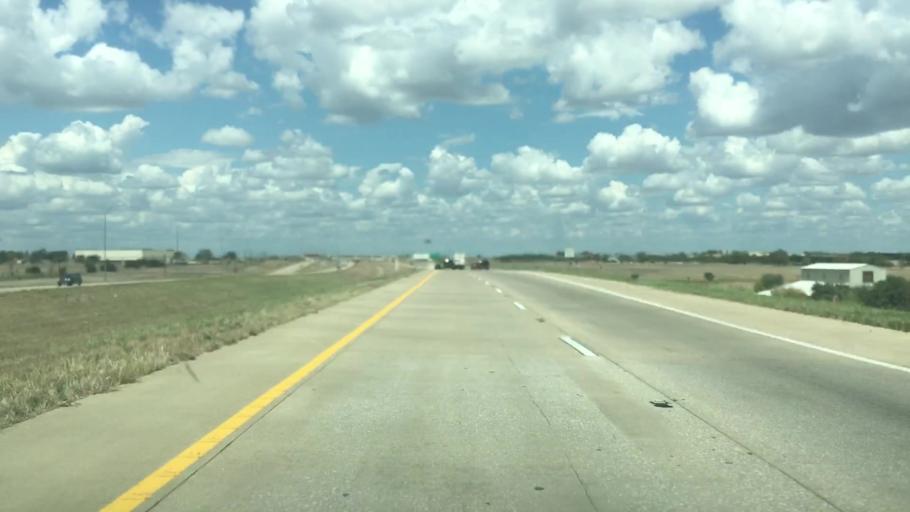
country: US
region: Texas
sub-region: Williamson County
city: Hutto
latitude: 30.5766
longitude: -97.5847
